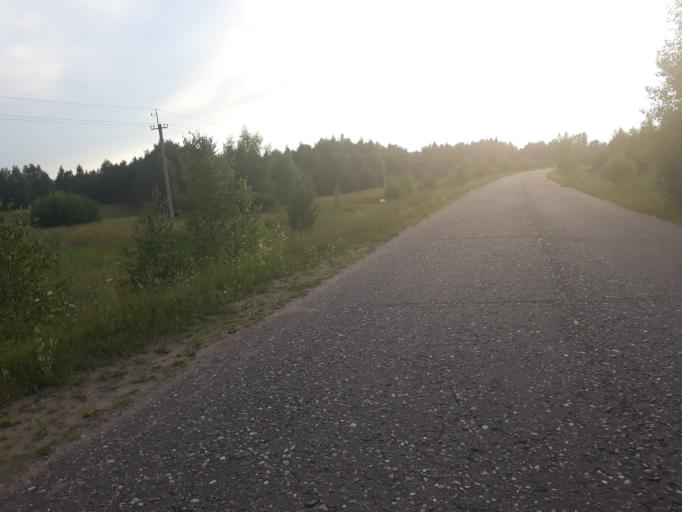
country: RU
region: Jaroslavl
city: Petrovsk
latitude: 56.8742
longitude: 39.0858
